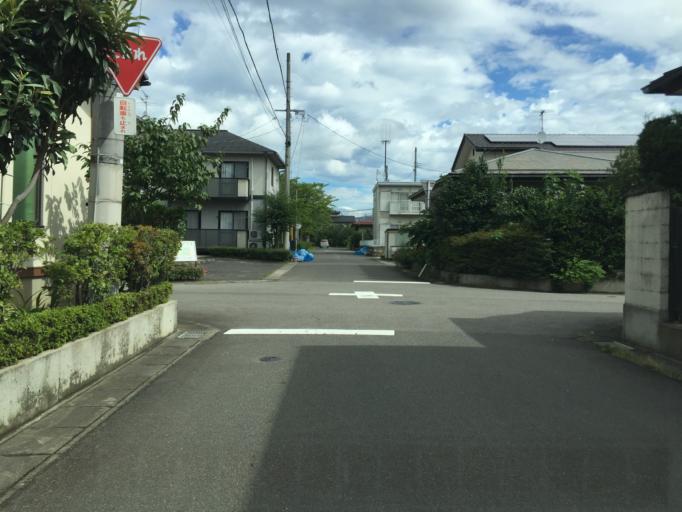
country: JP
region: Fukushima
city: Fukushima-shi
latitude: 37.7600
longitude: 140.4297
